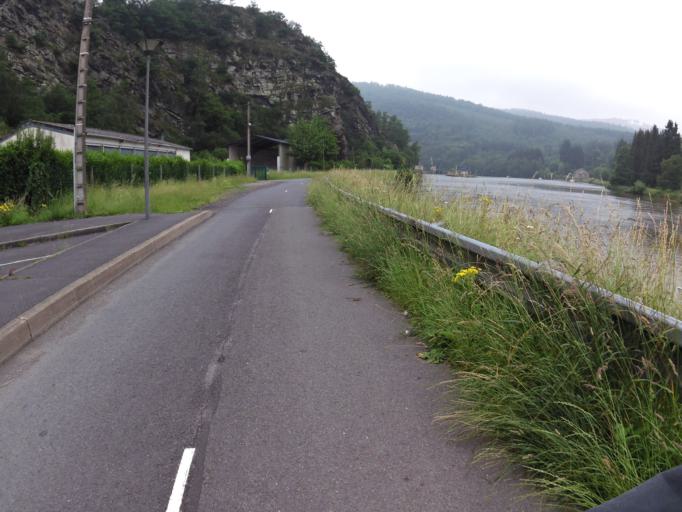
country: FR
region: Champagne-Ardenne
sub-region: Departement des Ardennes
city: Fumay
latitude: 49.9883
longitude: 4.7029
